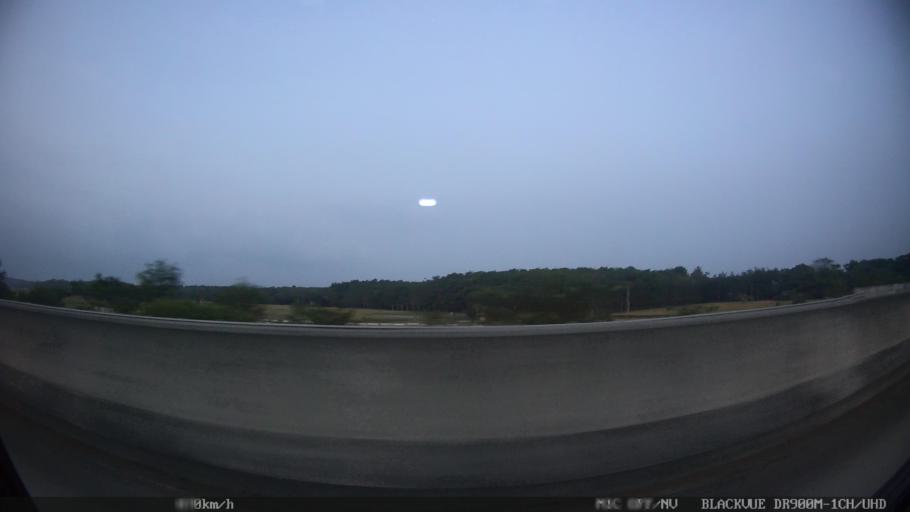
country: ID
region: Lampung
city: Sidorejo
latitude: -5.5926
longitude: 105.5484
